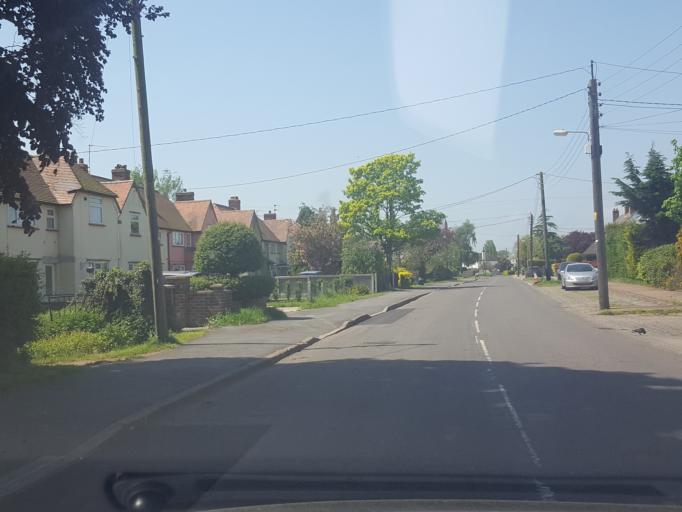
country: GB
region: England
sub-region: Essex
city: Great Bentley
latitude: 51.8550
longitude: 1.0597
